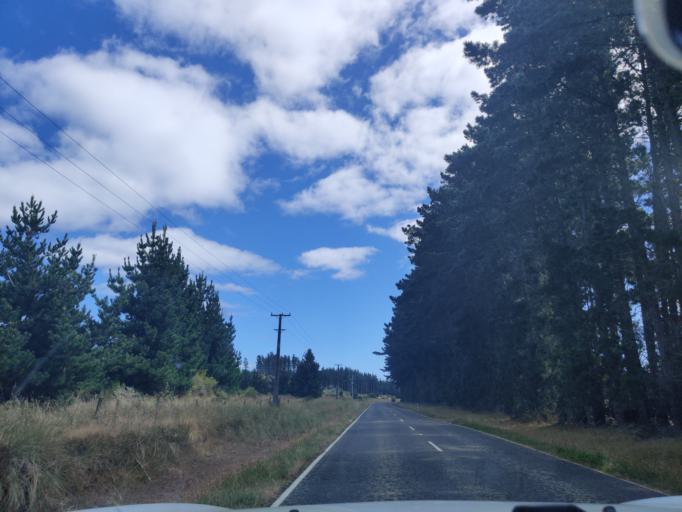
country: NZ
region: Manawatu-Wanganui
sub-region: Horowhenua District
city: Foxton
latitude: -40.3793
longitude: 175.2575
